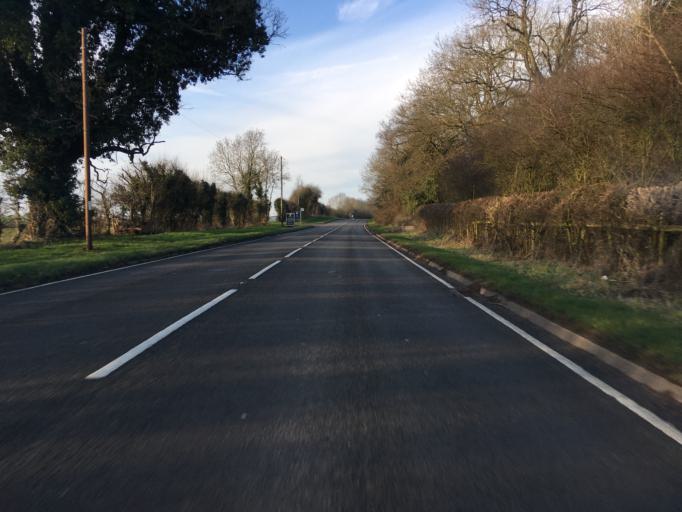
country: GB
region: England
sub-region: Warwickshire
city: Henley in Arden
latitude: 52.2586
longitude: -1.7640
